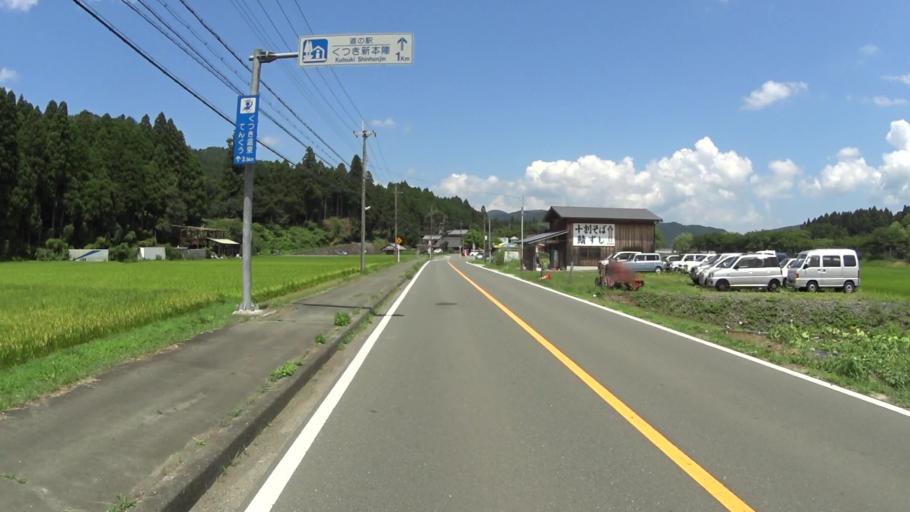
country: JP
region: Shiga Prefecture
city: Kitahama
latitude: 35.3437
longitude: 135.9088
